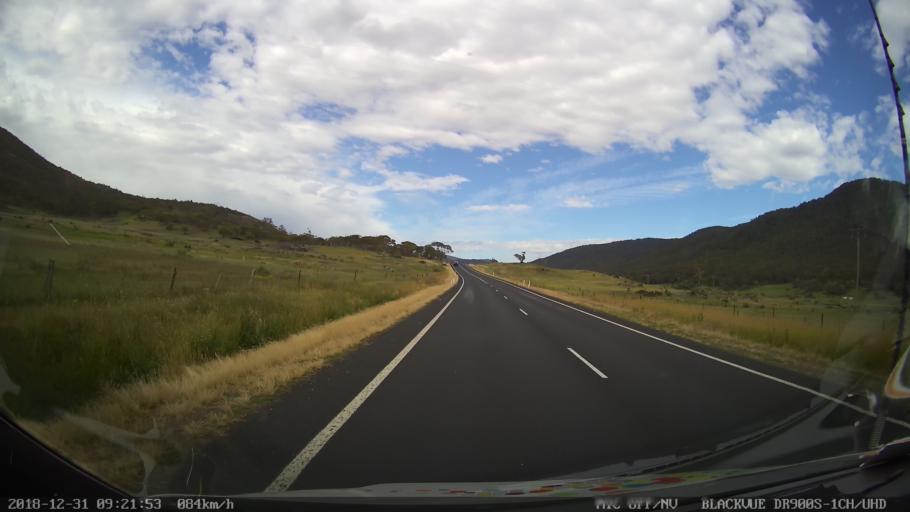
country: AU
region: New South Wales
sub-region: Snowy River
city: Jindabyne
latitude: -36.4315
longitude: 148.5556
